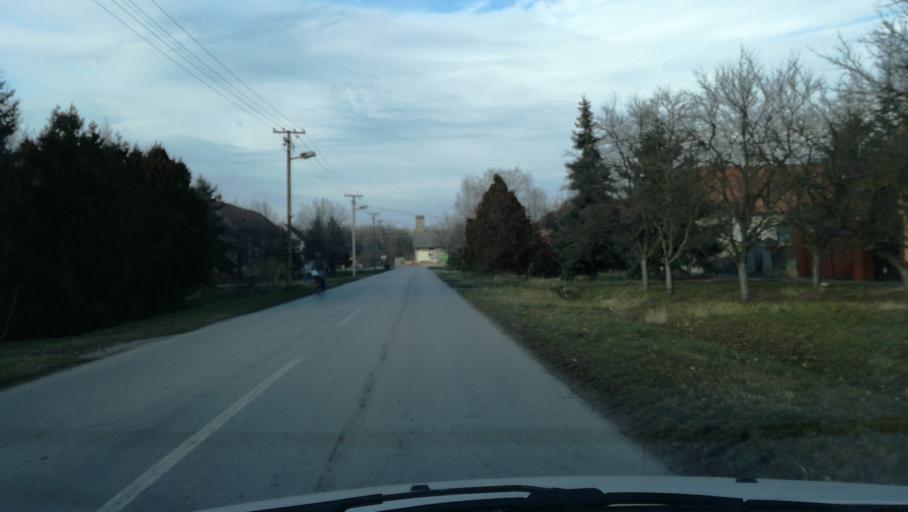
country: RS
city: Banatsko Veliko Selo
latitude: 45.8183
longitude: 20.6078
